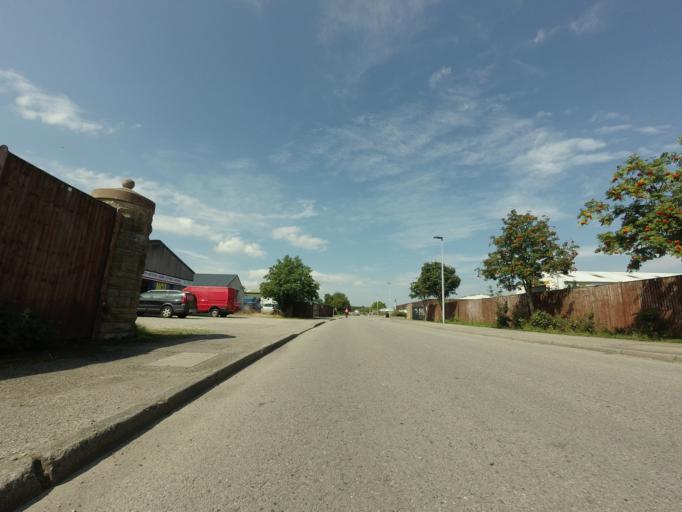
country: GB
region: Scotland
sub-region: Highland
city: Tain
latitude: 57.8156
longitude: -4.0577
